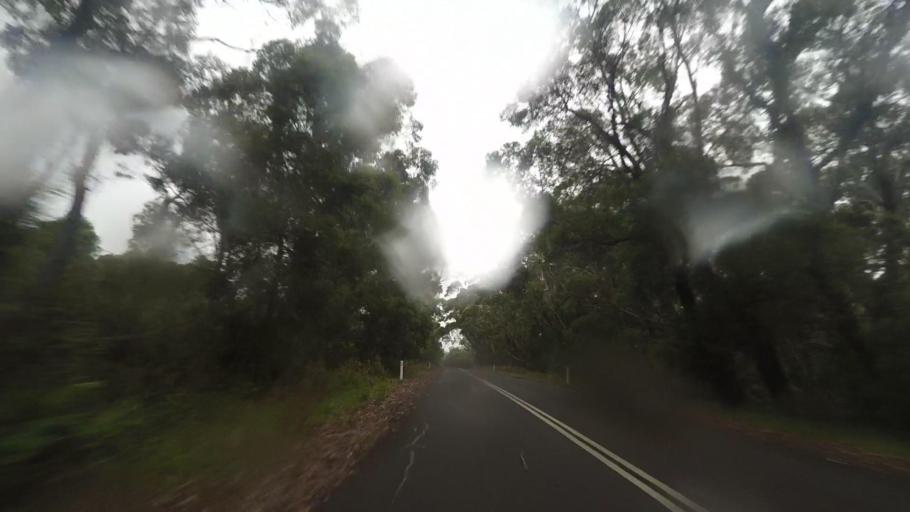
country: AU
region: New South Wales
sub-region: Wollongong
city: Mount Keira
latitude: -34.4009
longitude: 150.8400
